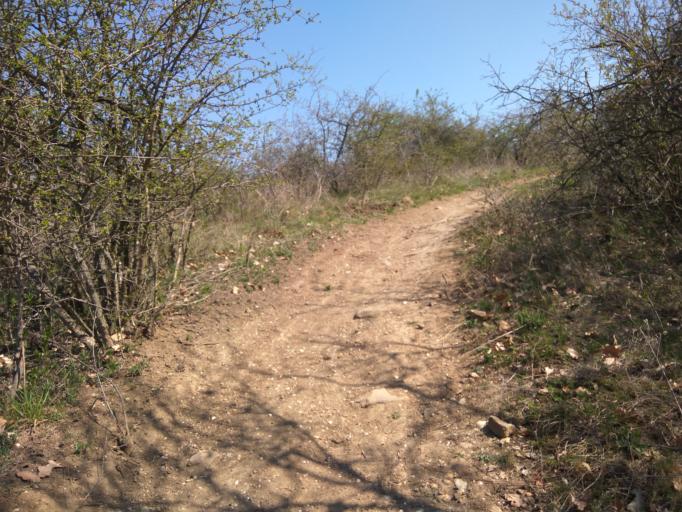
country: HU
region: Pest
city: Pomaz
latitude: 47.6271
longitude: 19.0154
